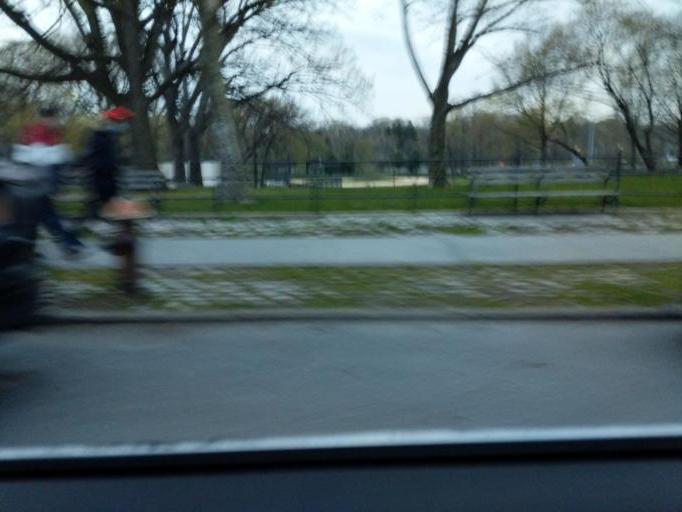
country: US
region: New York
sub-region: Bronx
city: The Bronx
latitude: 40.8522
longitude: -73.8687
